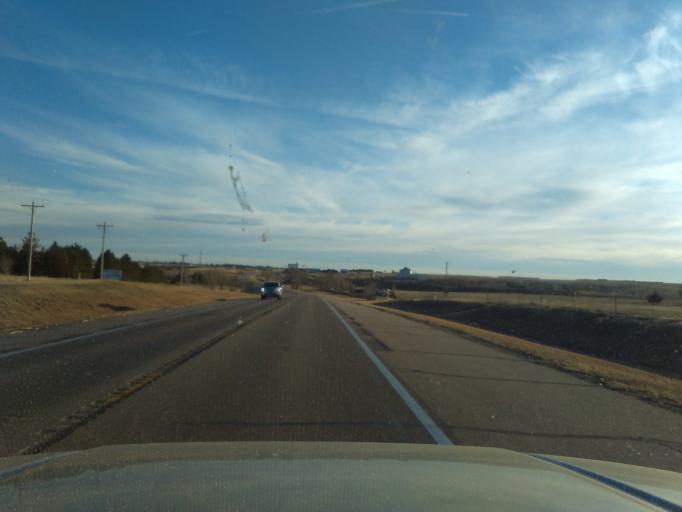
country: US
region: Kansas
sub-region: Logan County
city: Oakley
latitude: 39.1546
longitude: -100.8703
